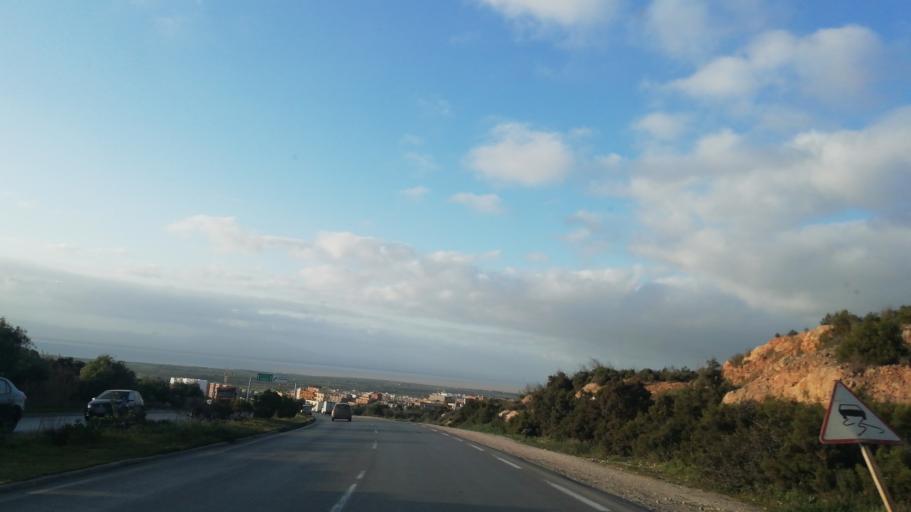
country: DZ
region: Oran
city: Es Senia
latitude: 35.6276
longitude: -0.7185
